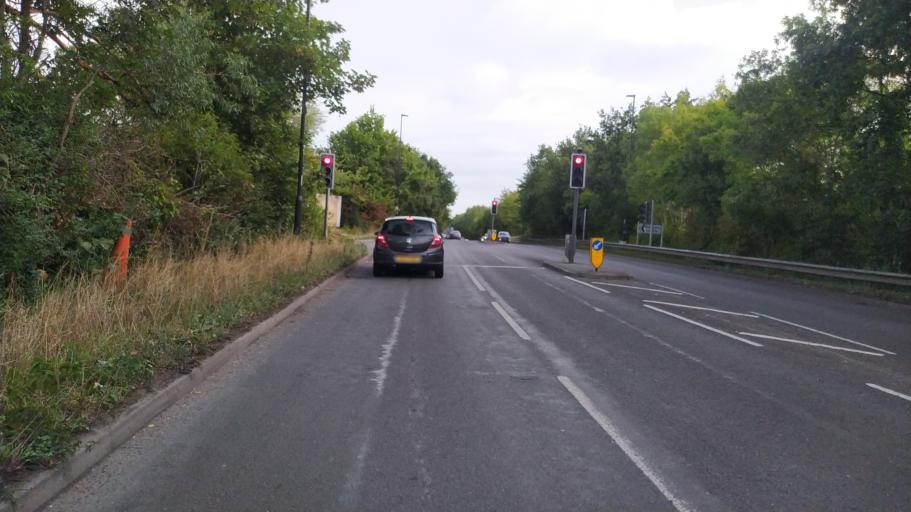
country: GB
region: England
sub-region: Southampton
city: Southampton
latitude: 50.9283
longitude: -1.3849
